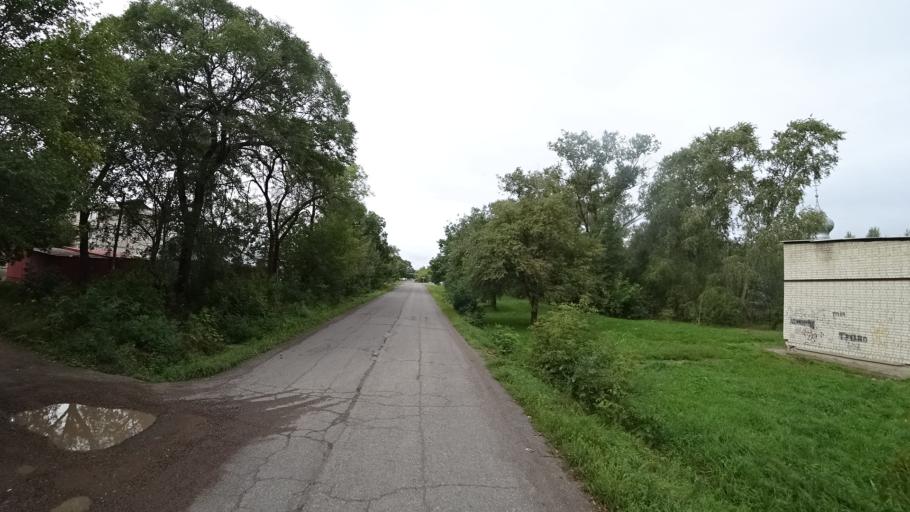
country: RU
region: Primorskiy
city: Chernigovka
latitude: 44.3407
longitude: 132.5830
